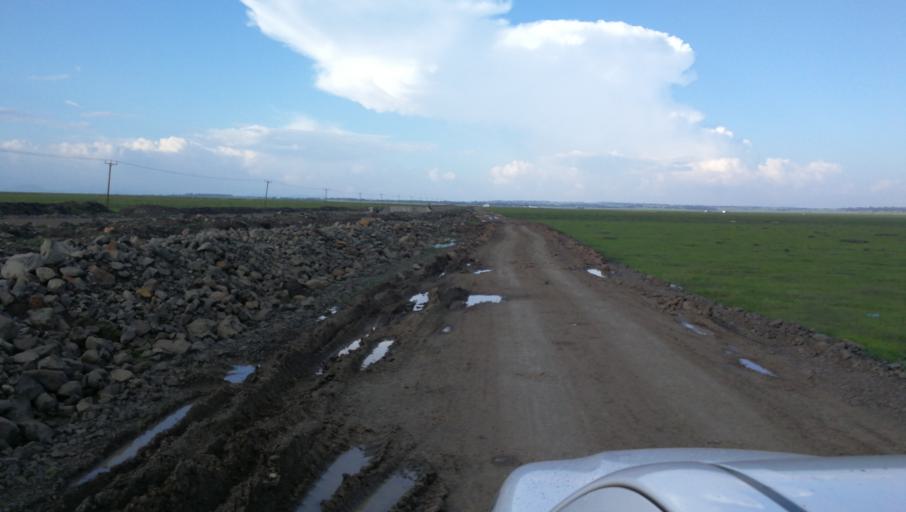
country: ET
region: Amhara
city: Were Ilu
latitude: 10.4828
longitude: 39.3004
